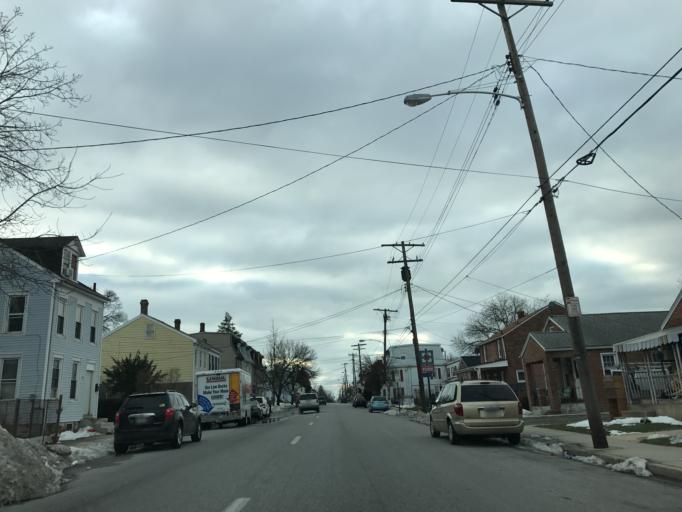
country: US
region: Pennsylvania
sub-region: York County
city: East York
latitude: 39.9739
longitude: -76.7041
